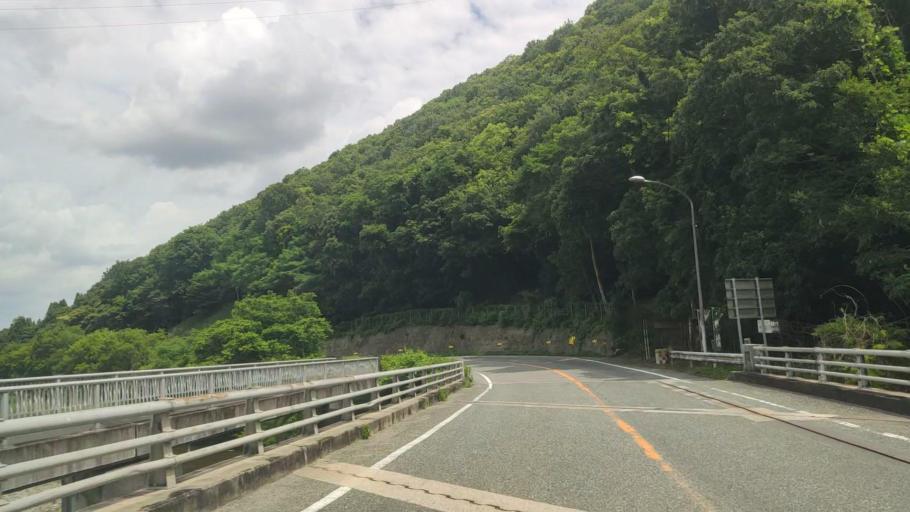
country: JP
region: Hyogo
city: Yamazakicho-nakabirose
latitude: 34.9407
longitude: 134.4961
